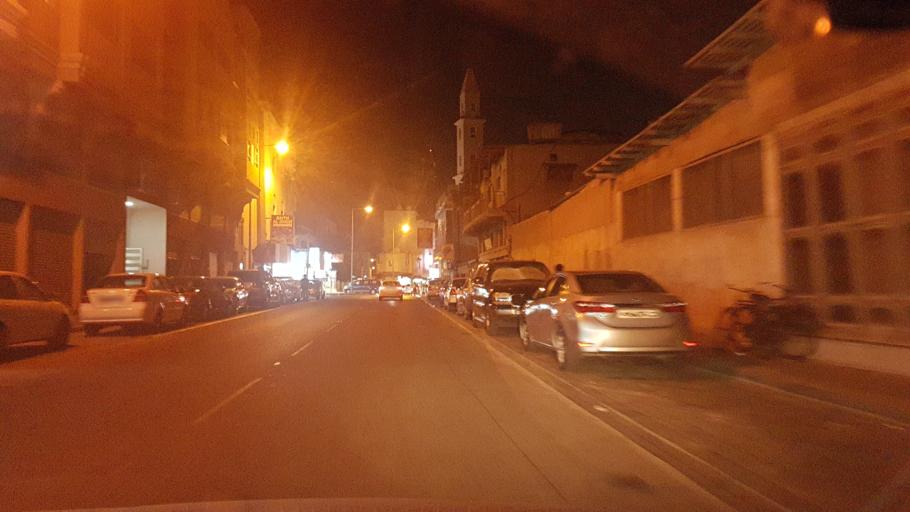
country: BH
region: Muharraq
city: Al Muharraq
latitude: 26.2717
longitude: 50.6092
